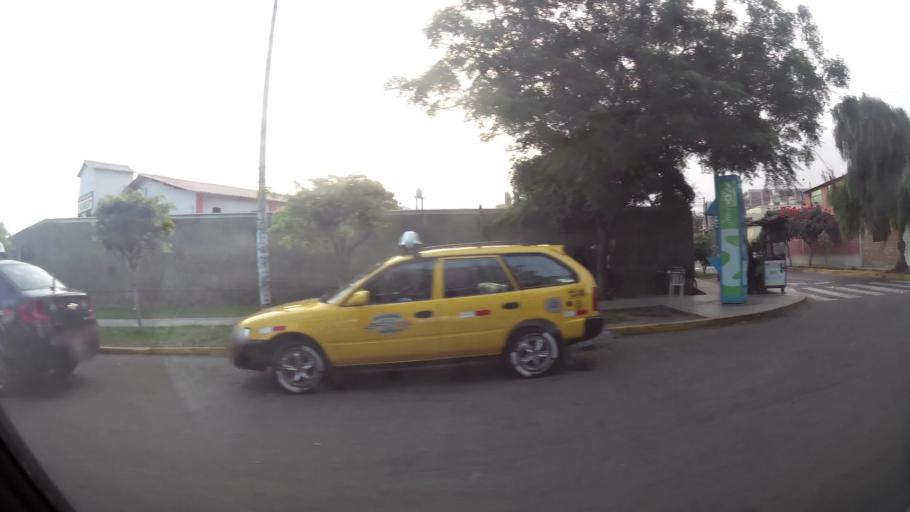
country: PE
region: La Libertad
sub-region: Provincia de Trujillo
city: Trujillo
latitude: -8.0989
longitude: -79.0345
